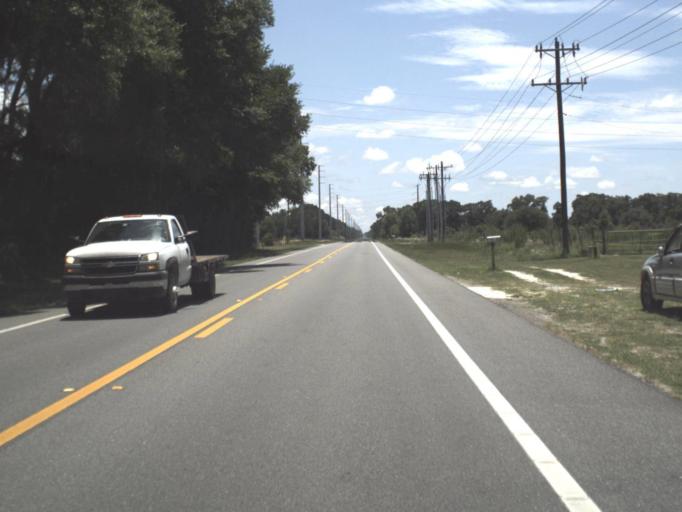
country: US
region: Florida
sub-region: Dixie County
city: Cross City
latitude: 29.7044
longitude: -82.9844
